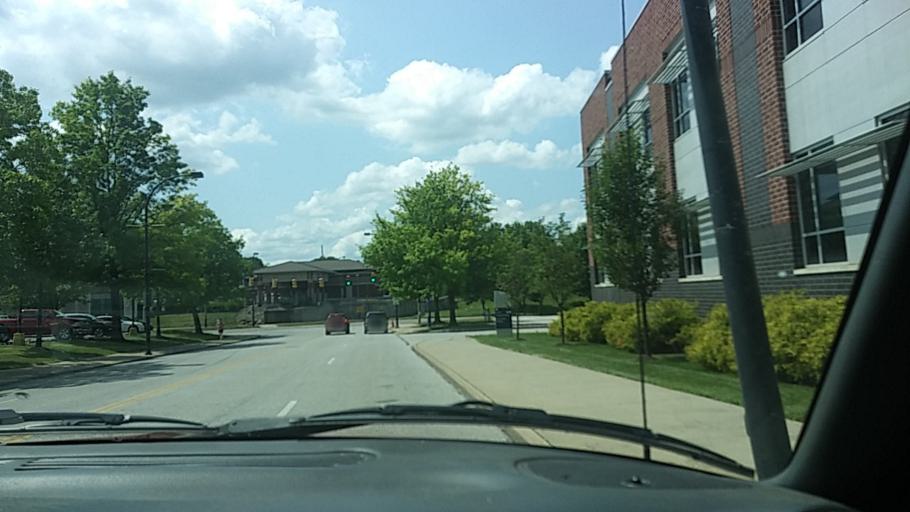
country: US
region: Ohio
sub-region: Summit County
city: Akron
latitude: 41.0761
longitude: -81.5168
